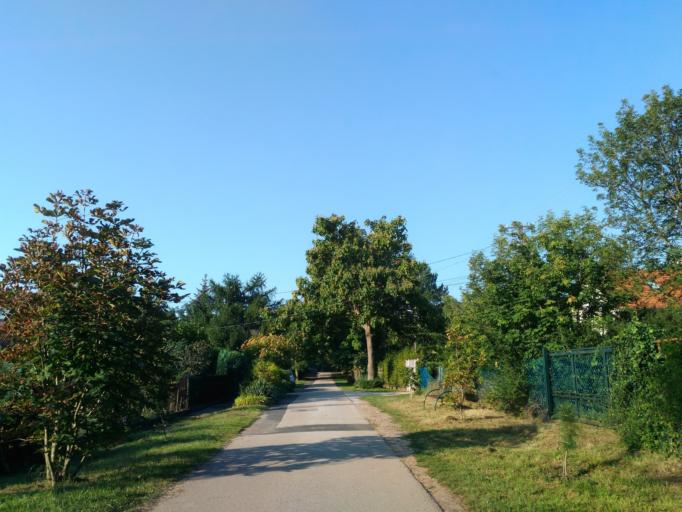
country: HU
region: Veszprem
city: Zanka
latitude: 46.8589
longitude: 17.6663
